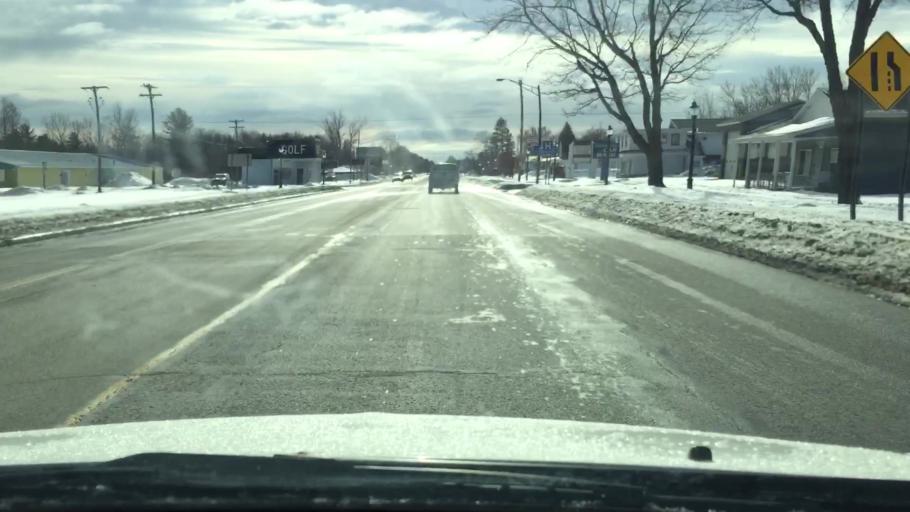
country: US
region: Michigan
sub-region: Kalkaska County
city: Kalkaska
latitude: 44.7293
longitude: -85.1796
